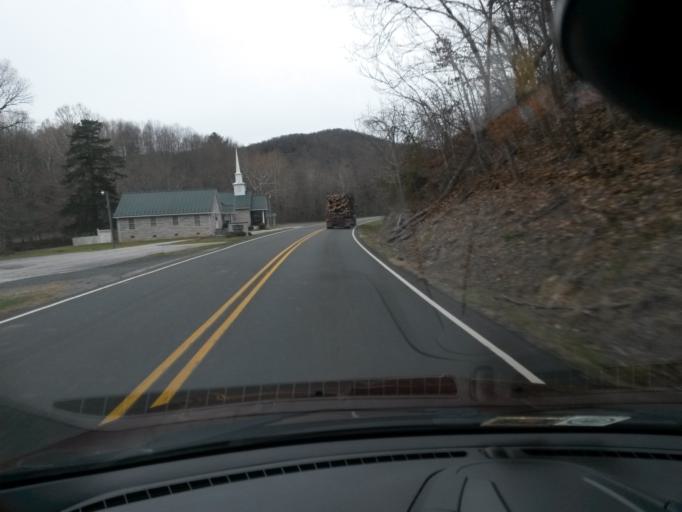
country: US
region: Virginia
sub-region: City of Buena Vista
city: Buena Vista
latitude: 37.6677
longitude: -79.2098
